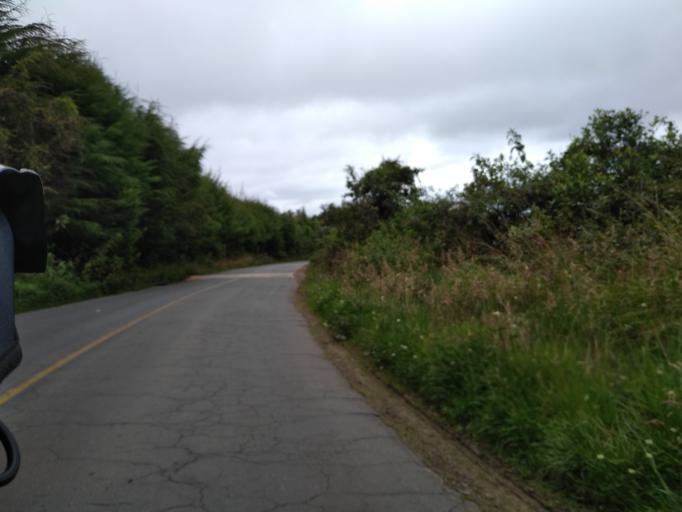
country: EC
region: Carchi
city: El Angel
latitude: 0.6312
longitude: -77.9306
